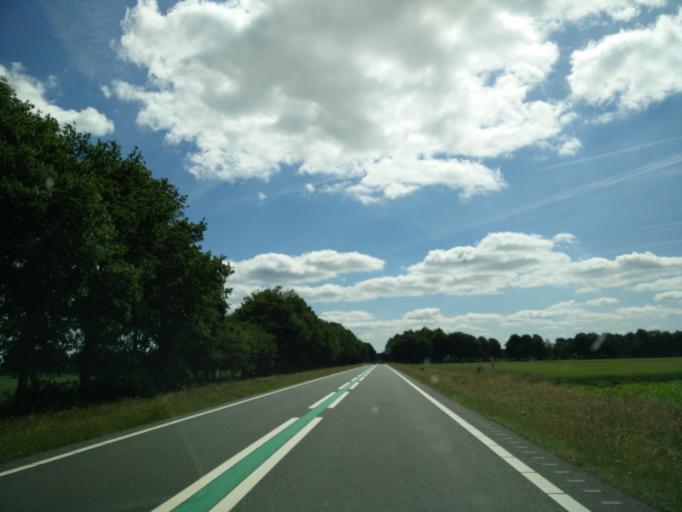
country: NL
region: Drenthe
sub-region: Gemeente Coevorden
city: Dalen
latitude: 52.8222
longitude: 6.6412
